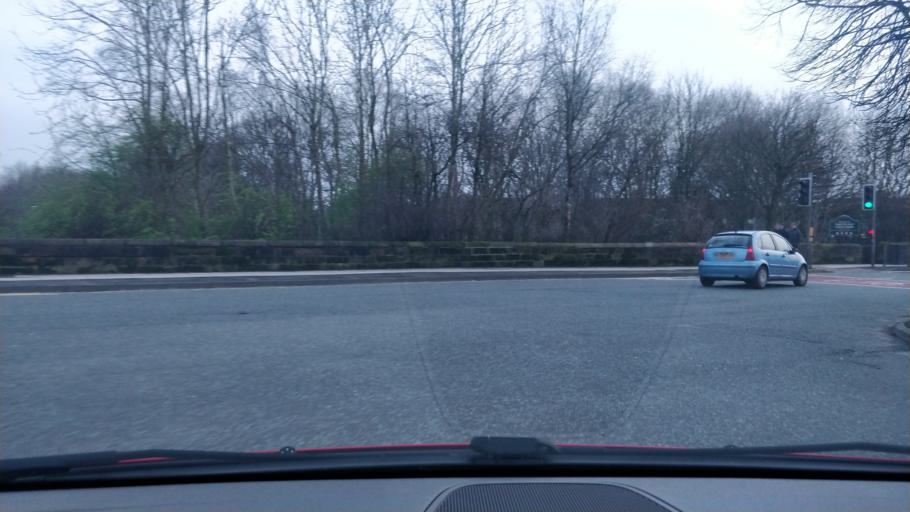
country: GB
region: England
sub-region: Knowsley
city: Huyton
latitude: 53.4206
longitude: -2.8480
